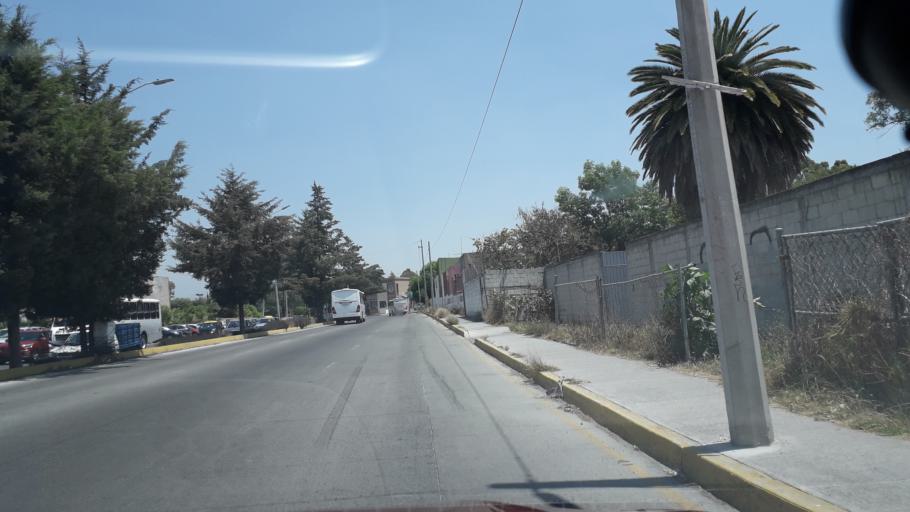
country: MX
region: Puebla
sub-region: Puebla
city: Galaxia la Calera
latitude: 19.0074
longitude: -98.1827
